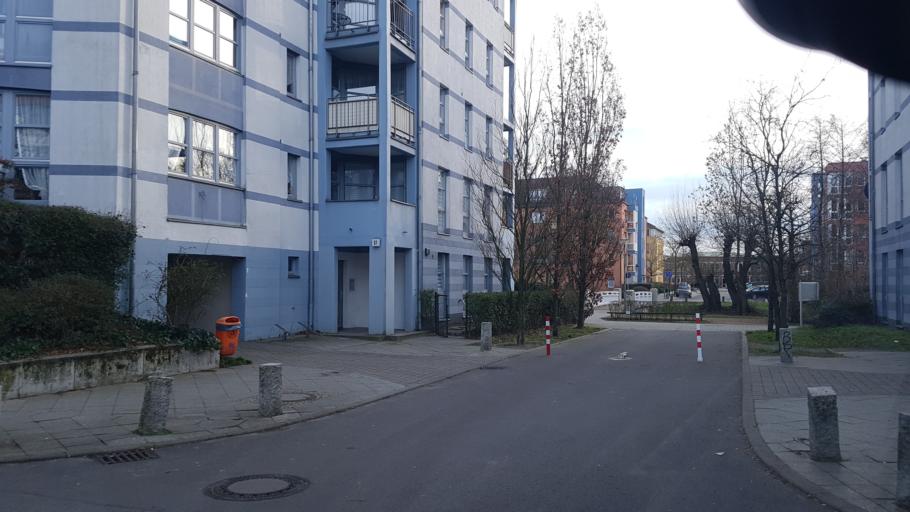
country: DE
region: Berlin
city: Wannsee
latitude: 52.3628
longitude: 13.1320
